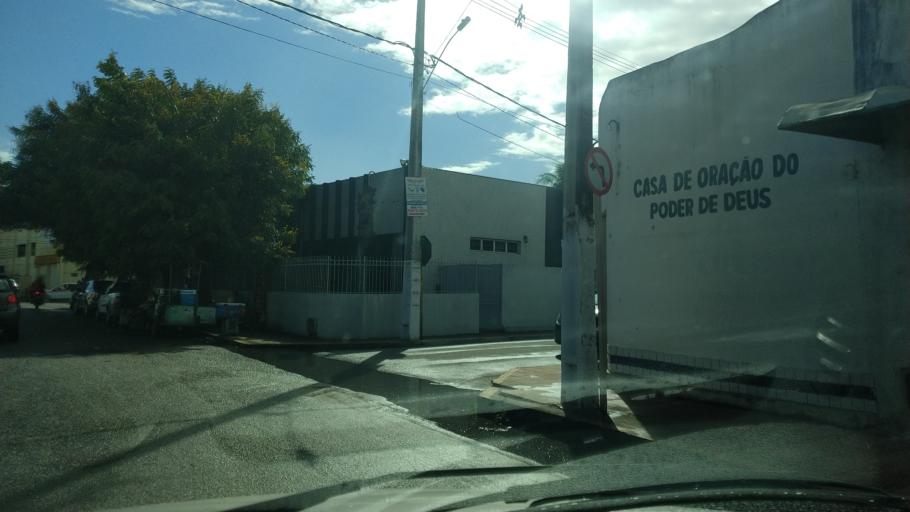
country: BR
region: Rio Grande do Norte
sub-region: Parnamirim
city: Parnamirim
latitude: -5.9153
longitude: -35.2617
